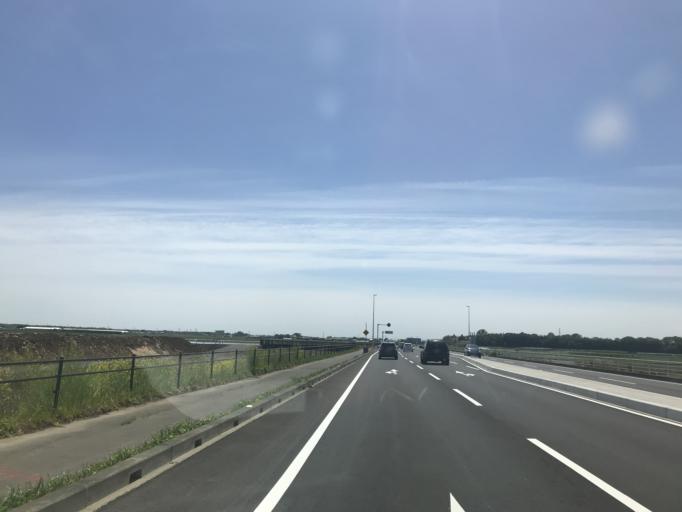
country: JP
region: Ibaraki
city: Shimodate
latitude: 36.2357
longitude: 139.9847
